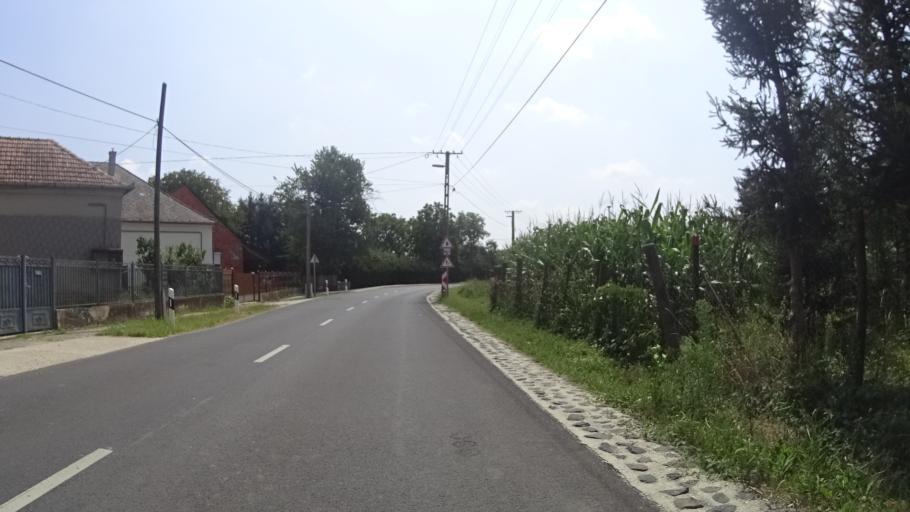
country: HU
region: Zala
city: Letenye
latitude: 46.4221
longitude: 16.7434
